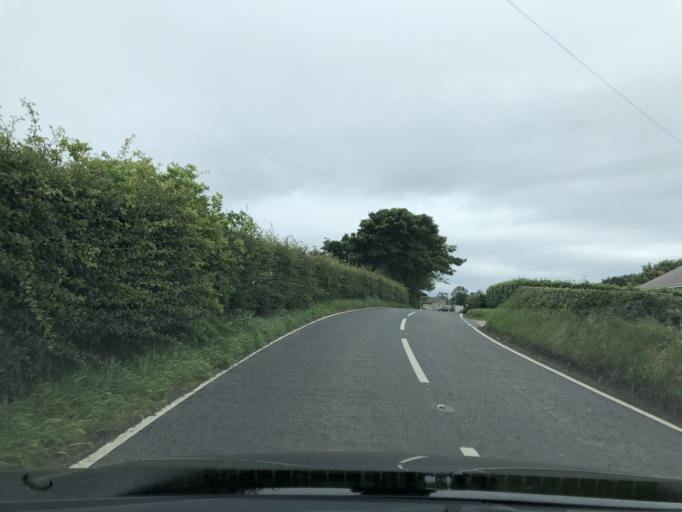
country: GB
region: Northern Ireland
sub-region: Down District
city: Dundrum
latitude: 54.2630
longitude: -5.7833
